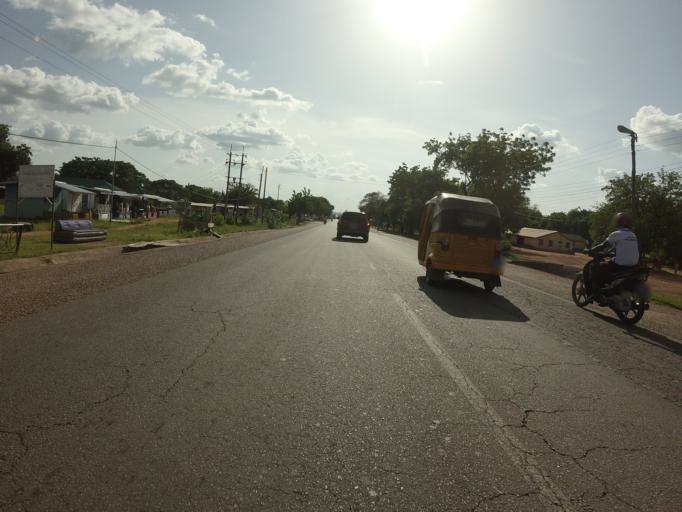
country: GH
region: Upper East
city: Bolgatanga
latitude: 10.8026
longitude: -0.8663
